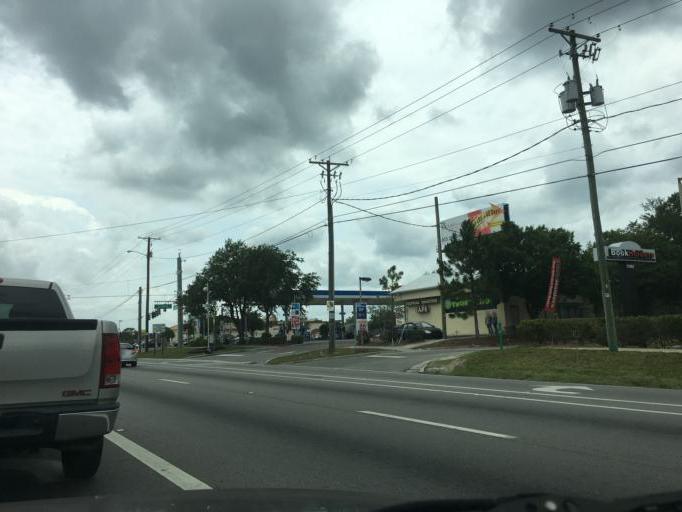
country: US
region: Florida
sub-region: Hillsborough County
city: University
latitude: 28.0555
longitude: -82.4261
